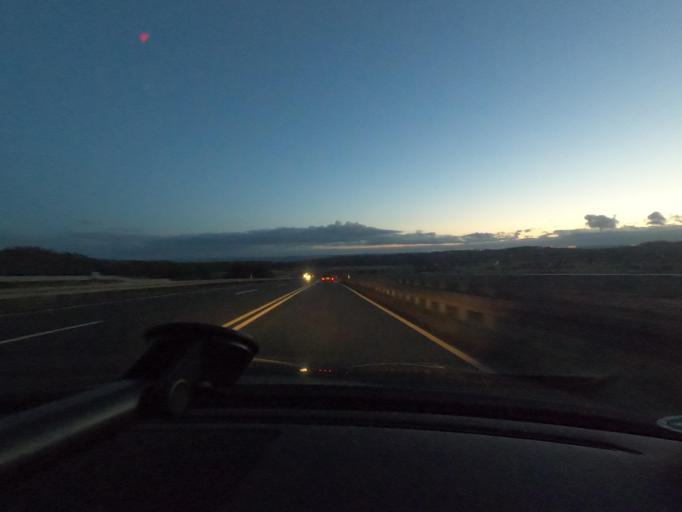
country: DE
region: Lower Saxony
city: Bad Sachsa
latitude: 51.5807
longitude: 10.5141
